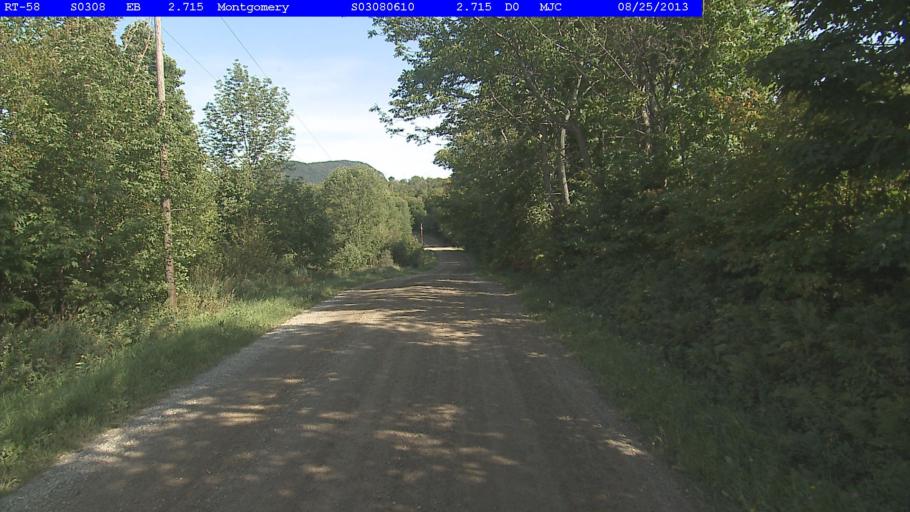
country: US
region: Vermont
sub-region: Franklin County
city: Richford
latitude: 44.8598
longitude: -72.5626
